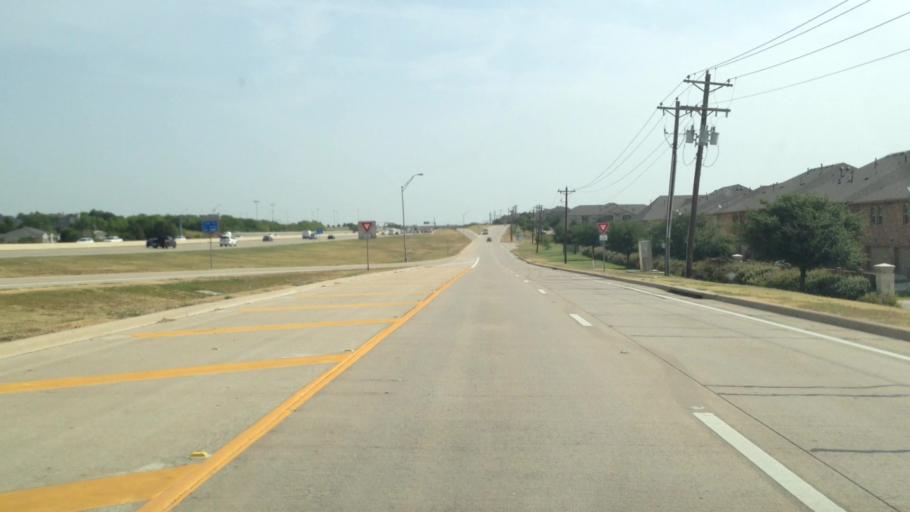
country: US
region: Texas
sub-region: Denton County
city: Lewisville
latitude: 33.0255
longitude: -96.9309
